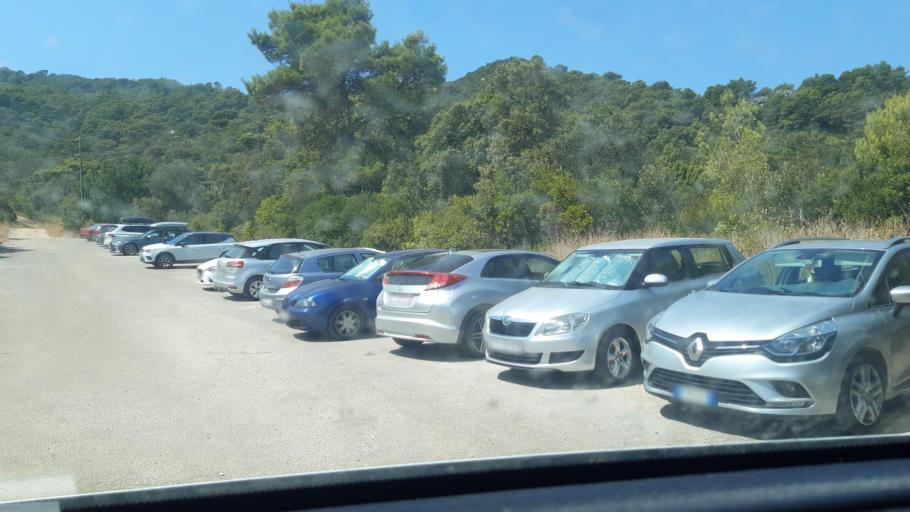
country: HR
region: Dubrovacko-Neretvanska
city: Ston
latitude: 42.7262
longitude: 17.6677
